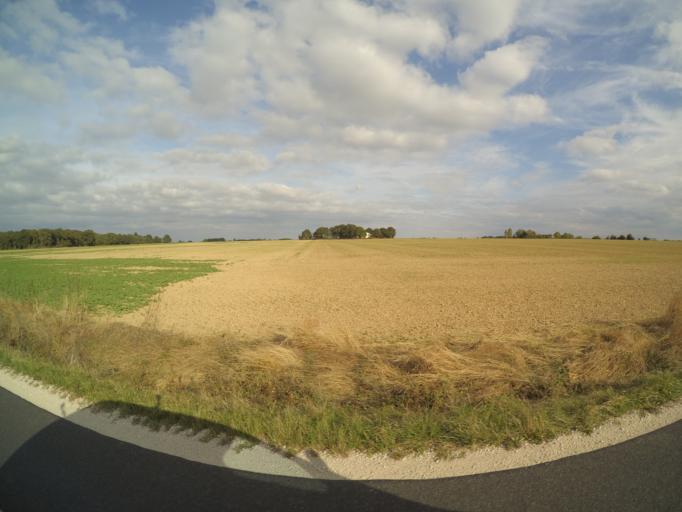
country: FR
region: Centre
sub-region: Departement d'Indre-et-Loire
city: Nazelles-Negron
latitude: 47.4508
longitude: 0.9560
